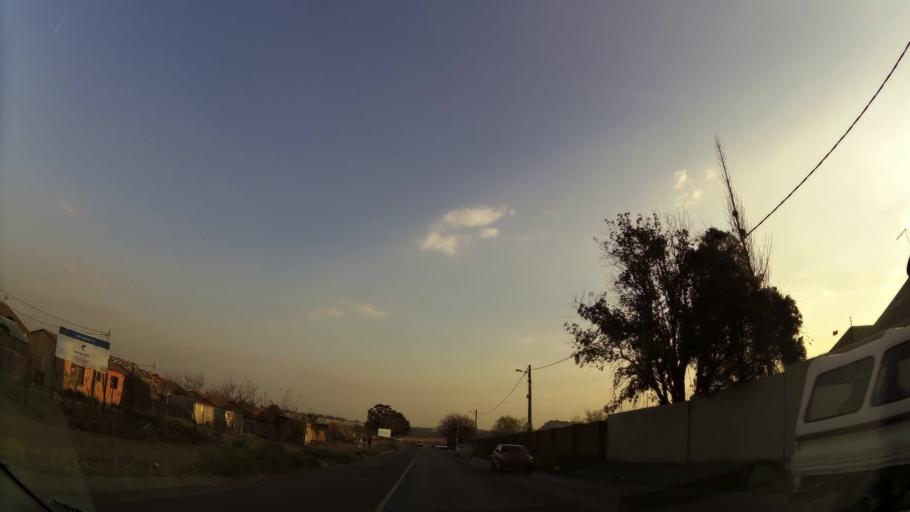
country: ZA
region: Gauteng
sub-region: Ekurhuleni Metropolitan Municipality
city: Benoni
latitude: -26.1604
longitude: 28.3736
